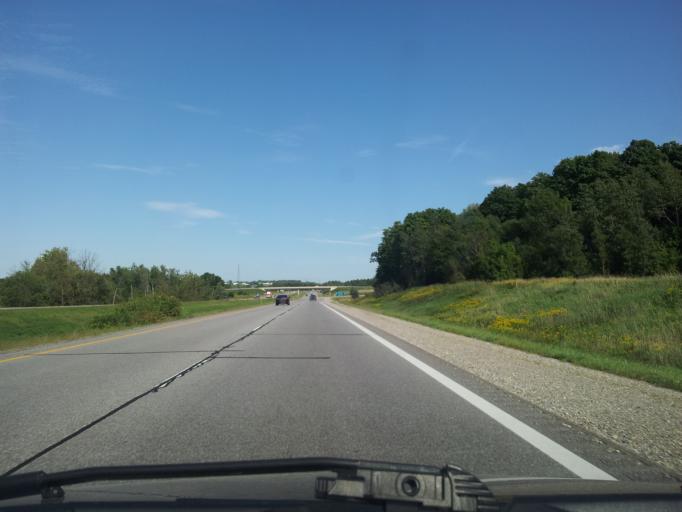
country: CA
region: Ontario
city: Kitchener
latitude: 43.4035
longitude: -80.6058
